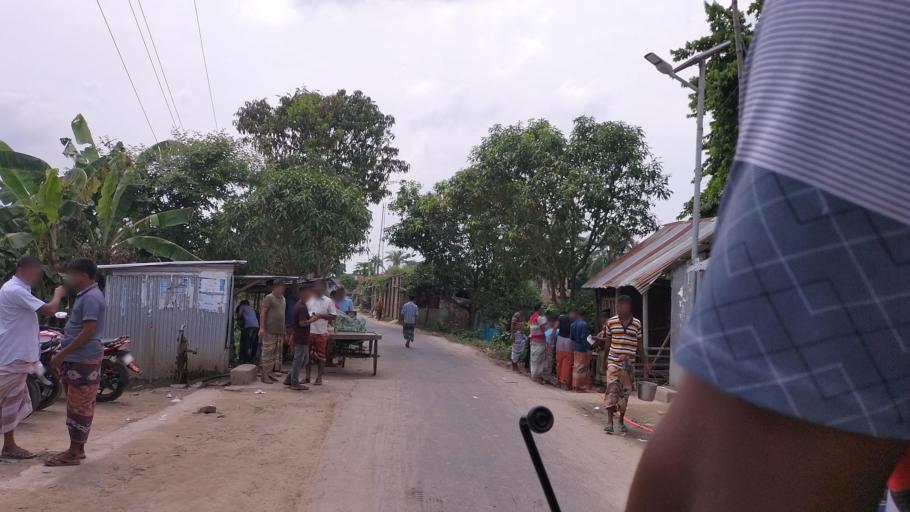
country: BD
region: Rajshahi
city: Rajshahi
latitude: 24.5255
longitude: 88.6151
